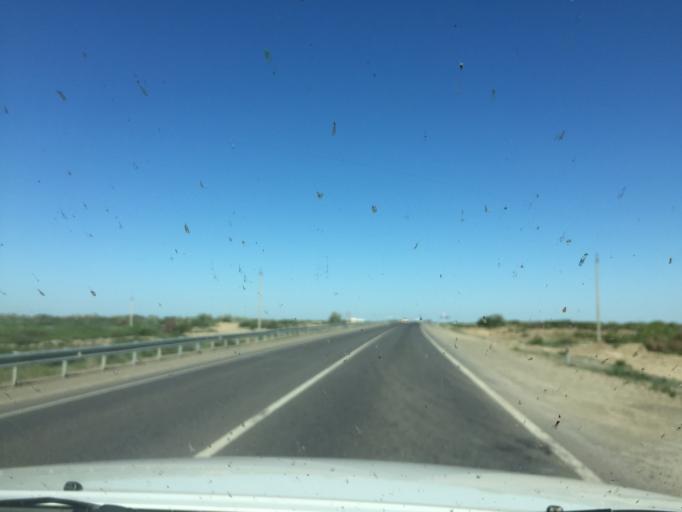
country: KZ
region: Qyzylorda
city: Terenozek
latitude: 44.8982
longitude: 64.9927
